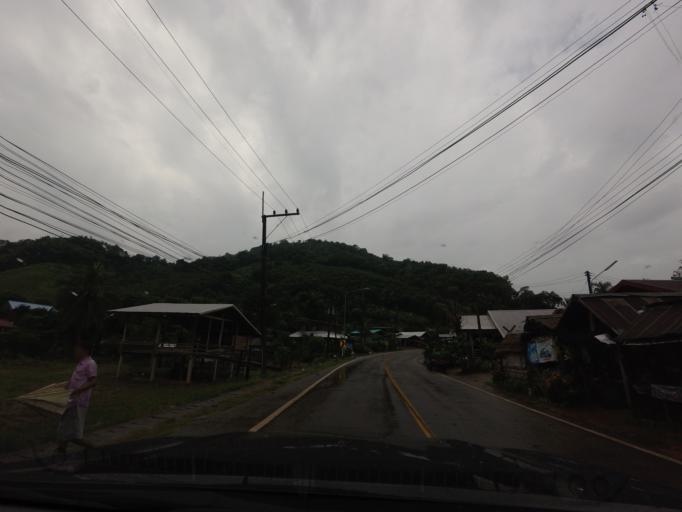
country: TH
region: Nong Khai
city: Sangkhom
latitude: 18.2041
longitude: 102.1179
